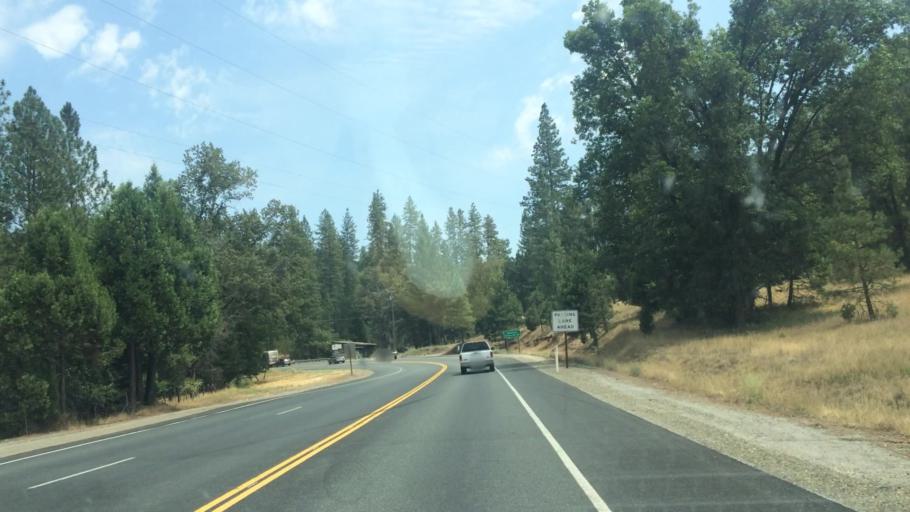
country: US
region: California
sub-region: Amador County
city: Pine Grove
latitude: 38.4002
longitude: -120.6352
